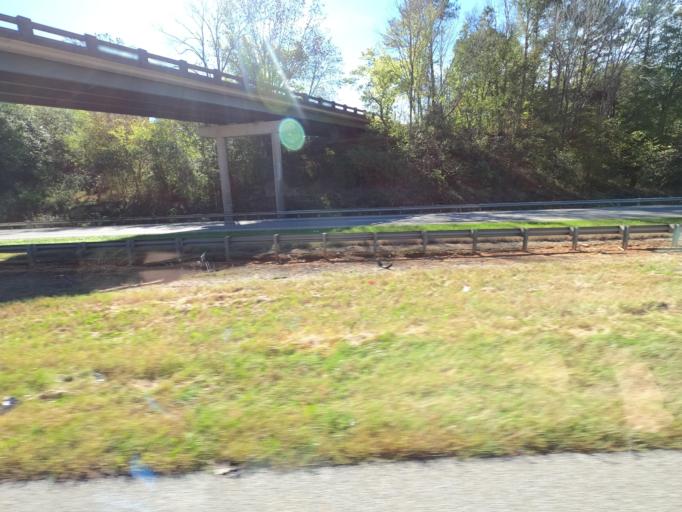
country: US
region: Tennessee
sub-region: Dickson County
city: Burns
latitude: 36.0180
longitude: -87.2420
